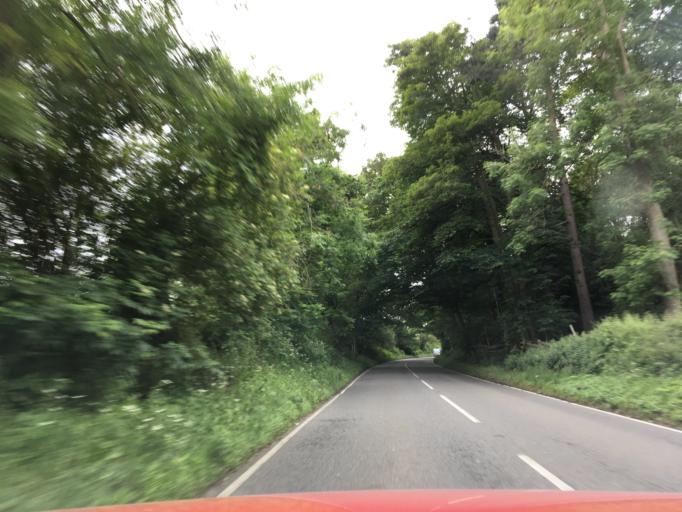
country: GB
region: England
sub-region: Central Bedfordshire
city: Woburn
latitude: 51.9835
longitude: -0.6348
